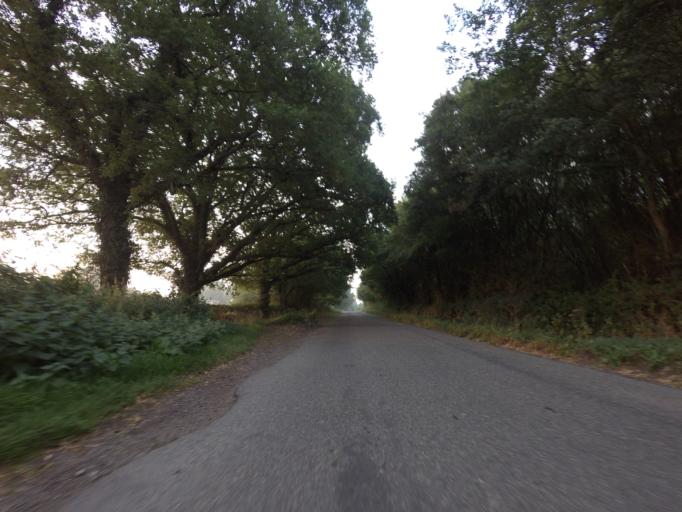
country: GB
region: England
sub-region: Kent
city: Lenham
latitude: 51.1805
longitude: 0.7241
